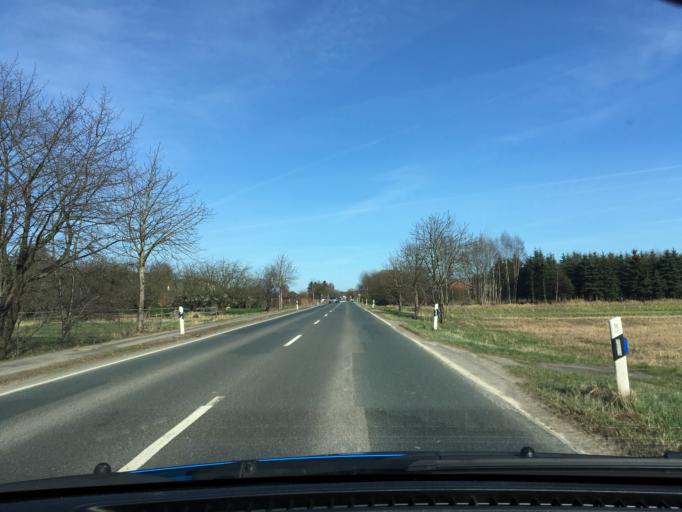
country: DE
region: Lower Saxony
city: Drage
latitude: 53.4184
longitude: 10.2745
